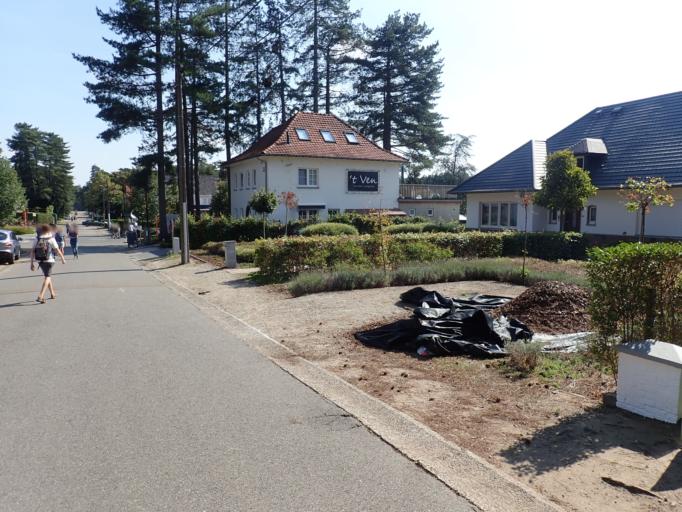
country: BE
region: Flanders
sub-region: Provincie Vlaams-Brabant
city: Scherpenheuvel-Zichem
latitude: 51.0284
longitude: 4.9833
